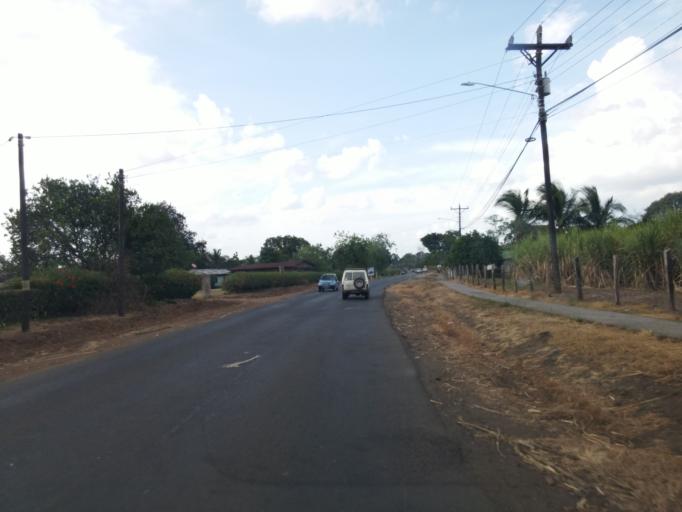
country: CR
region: Alajuela
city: Quesada
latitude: 10.4020
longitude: -84.4732
